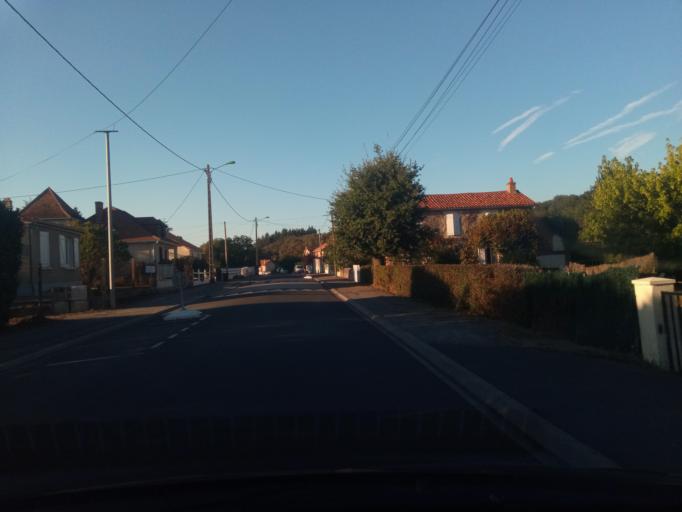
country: FR
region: Poitou-Charentes
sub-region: Departement de la Vienne
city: Montmorillon
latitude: 46.4112
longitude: 0.8806
